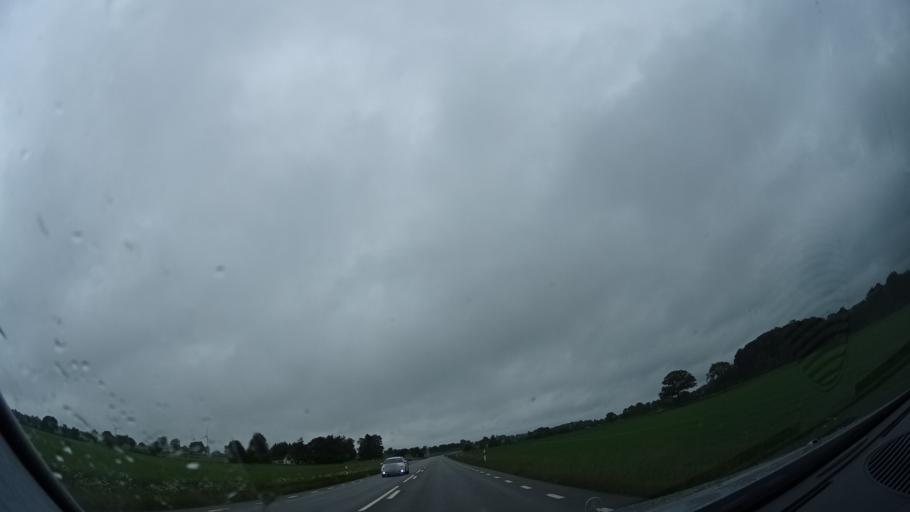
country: SE
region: Skane
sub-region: Hoors Kommun
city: Loberod
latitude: 55.8264
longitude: 13.4874
